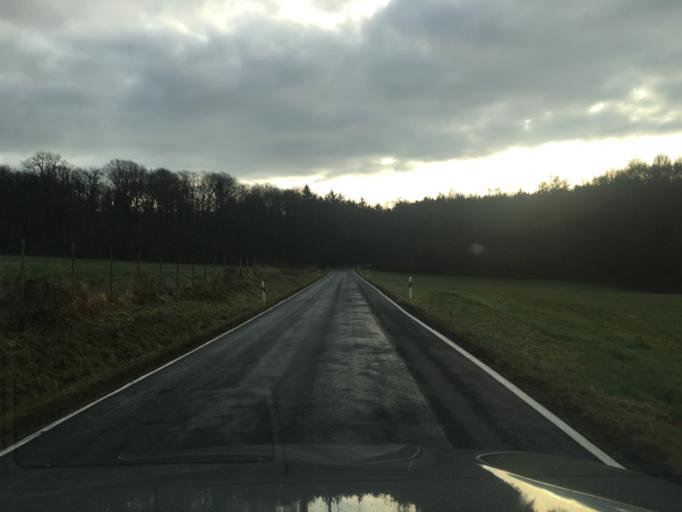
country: DE
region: Rheinland-Pfalz
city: Unkel
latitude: 50.5842
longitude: 7.1684
